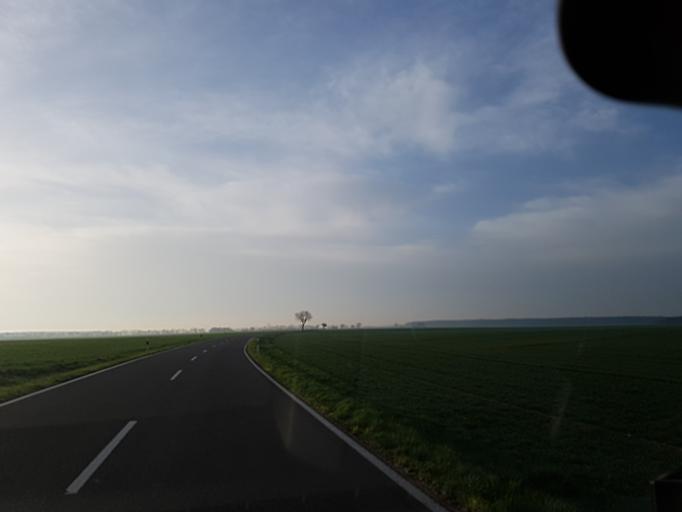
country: DE
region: Brandenburg
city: Muhlberg
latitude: 51.4007
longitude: 13.2615
